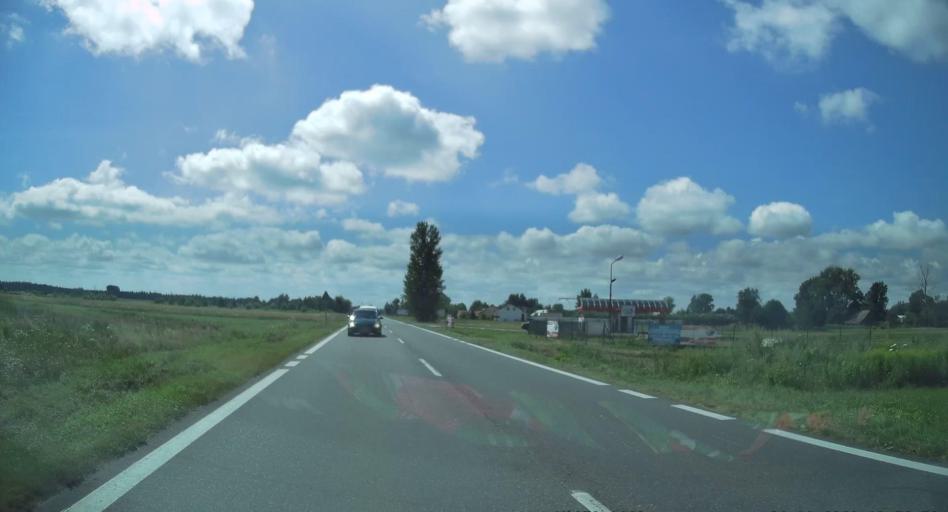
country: PL
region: Subcarpathian Voivodeship
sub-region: Powiat mielecki
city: Padew Narodowa
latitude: 50.4258
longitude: 21.4860
